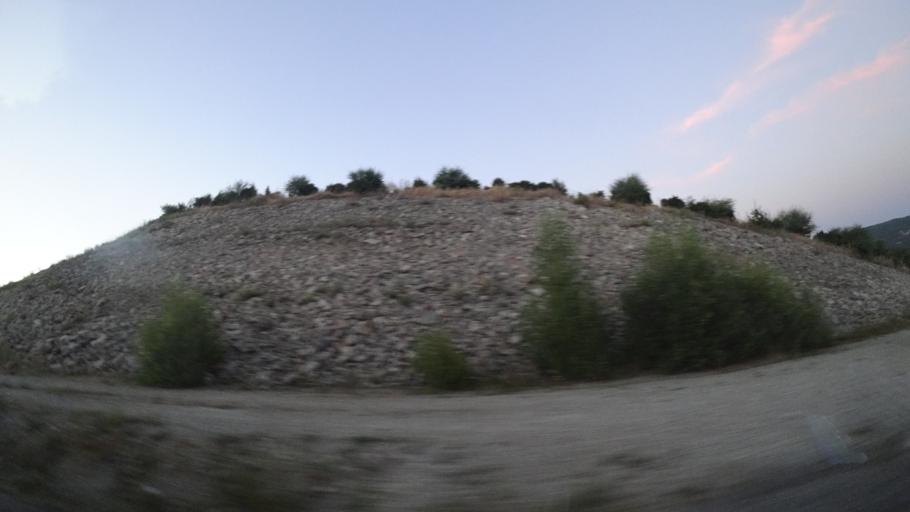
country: FR
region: Midi-Pyrenees
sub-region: Departement de l'Aveyron
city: Millau
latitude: 44.1223
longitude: 3.0565
